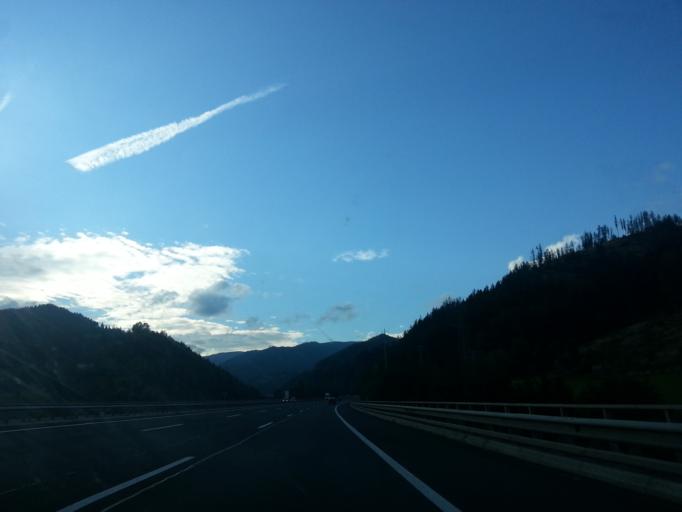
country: AT
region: Styria
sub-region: Politischer Bezirk Graz-Umgebung
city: Ubelbach
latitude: 47.2300
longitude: 15.2167
